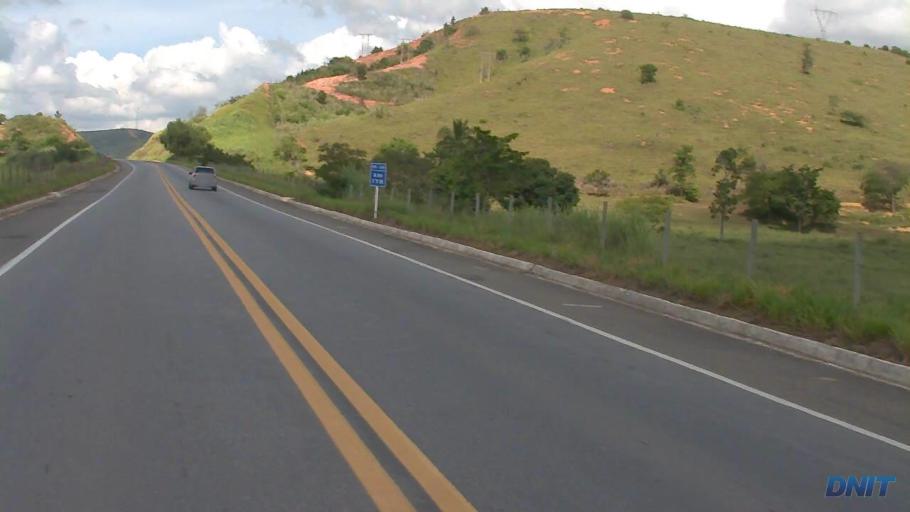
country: BR
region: Minas Gerais
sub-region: Governador Valadares
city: Governador Valadares
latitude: -19.0045
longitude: -42.1299
